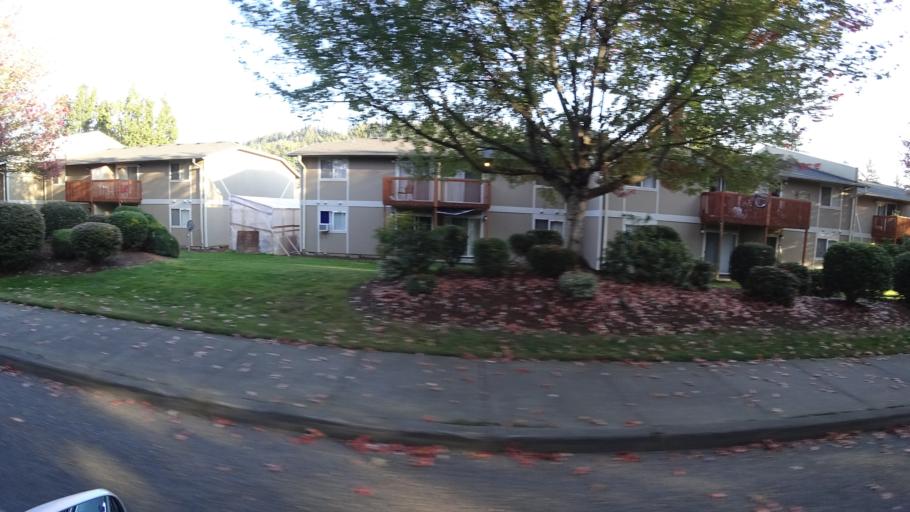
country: US
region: Oregon
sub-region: Multnomah County
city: Gresham
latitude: 45.4920
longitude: -122.4468
